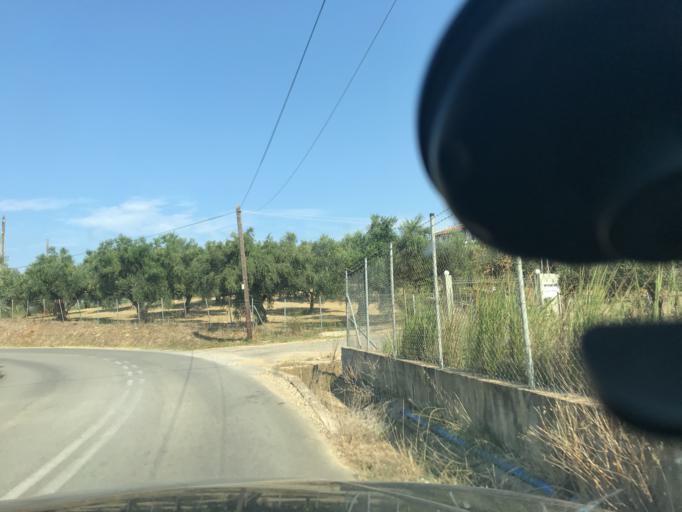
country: GR
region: West Greece
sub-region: Nomos Ileias
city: Kardamas
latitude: 37.7158
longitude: 21.3421
